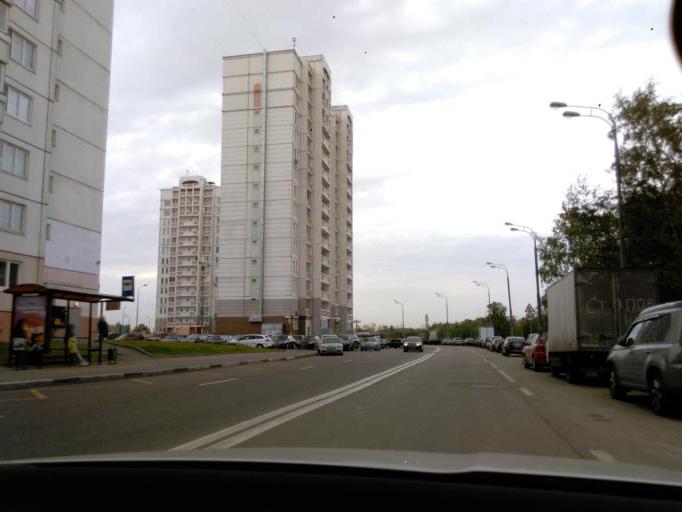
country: RU
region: Moscow
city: Severnyy
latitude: 55.9277
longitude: 37.5415
